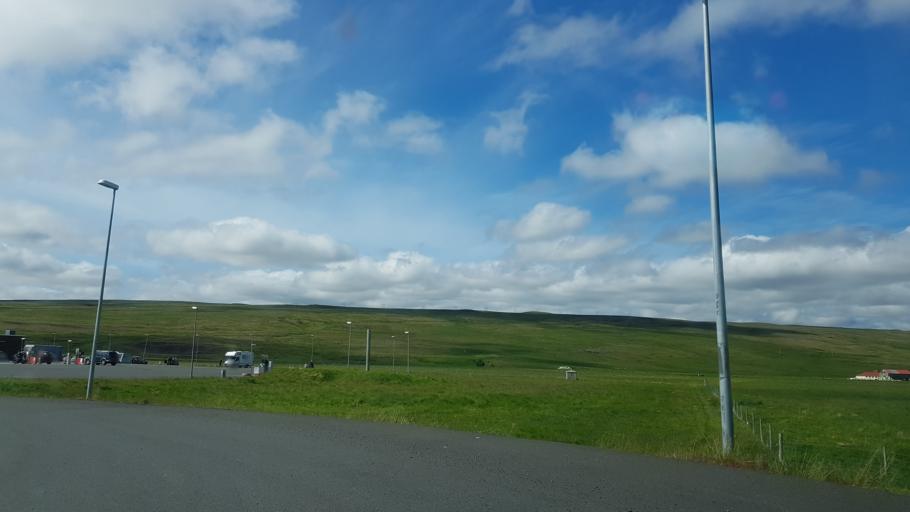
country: IS
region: West
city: Borgarnes
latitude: 65.1451
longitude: -21.0813
